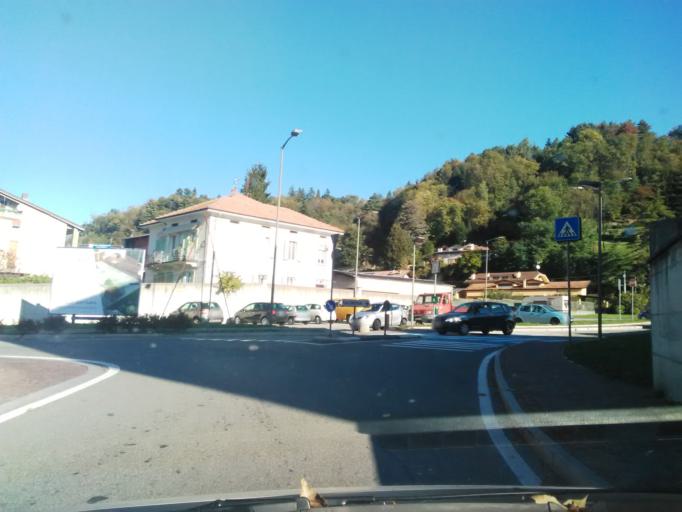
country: IT
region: Piedmont
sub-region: Provincia di Vercelli
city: Borgosesia
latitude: 45.7219
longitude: 8.2709
